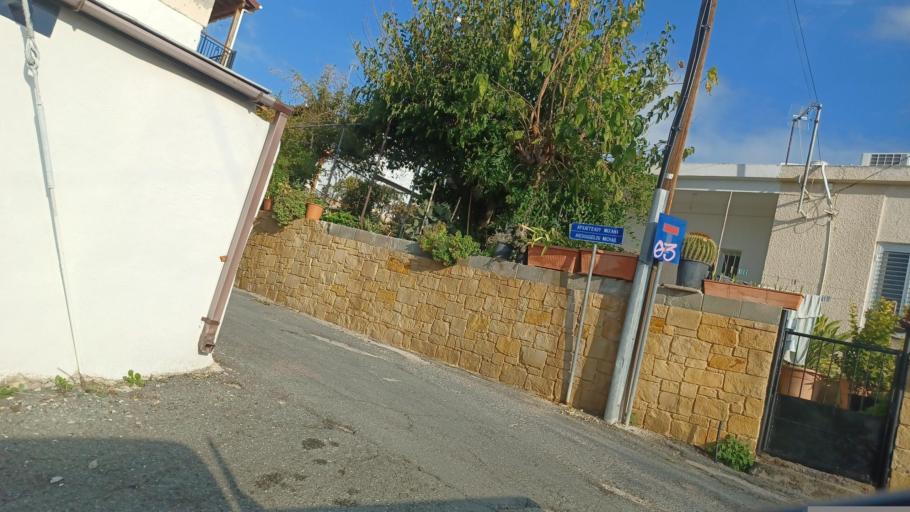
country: CY
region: Pafos
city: Mesogi
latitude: 34.7913
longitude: 32.4878
